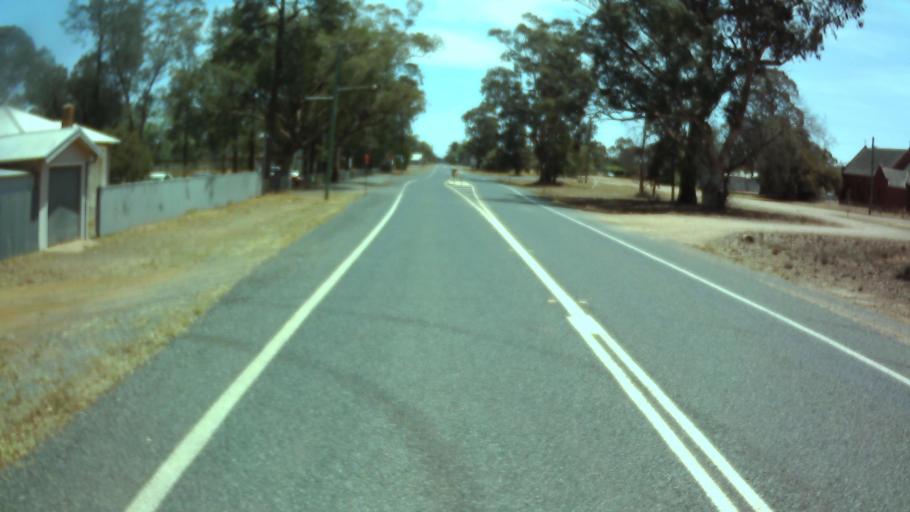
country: AU
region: New South Wales
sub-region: Weddin
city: Grenfell
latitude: -33.8446
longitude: 147.7453
